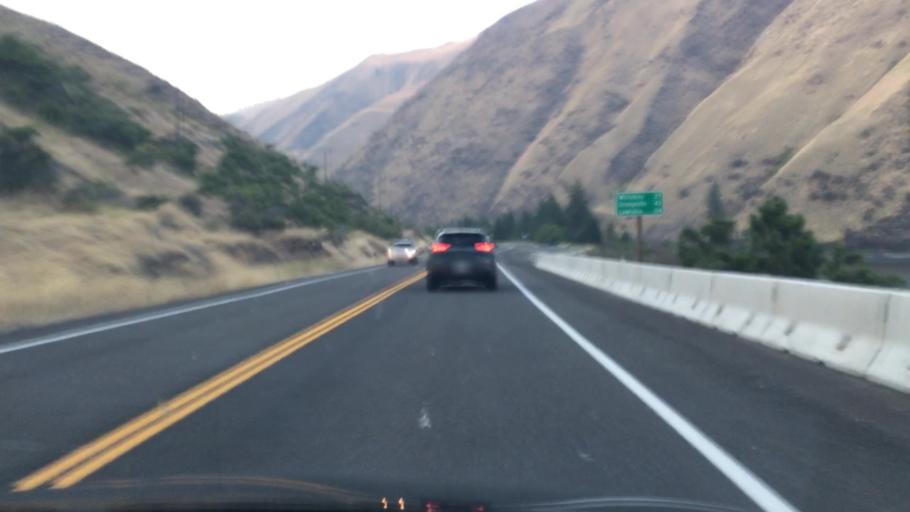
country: US
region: Idaho
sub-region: Idaho County
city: Grangeville
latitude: 45.4378
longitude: -116.3173
